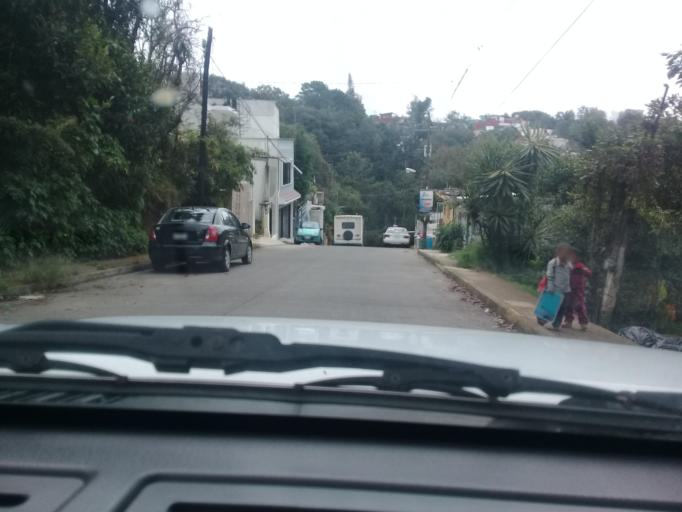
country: MX
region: Veracruz
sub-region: Xalapa
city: Xalapa de Enriquez
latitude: 19.5105
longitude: -96.9113
